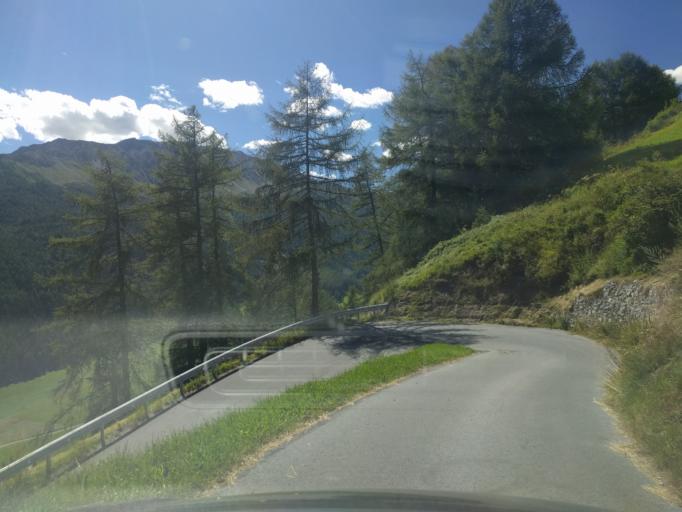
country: IT
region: Trentino-Alto Adige
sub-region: Bolzano
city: Tubre
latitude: 46.6069
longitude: 10.4096
